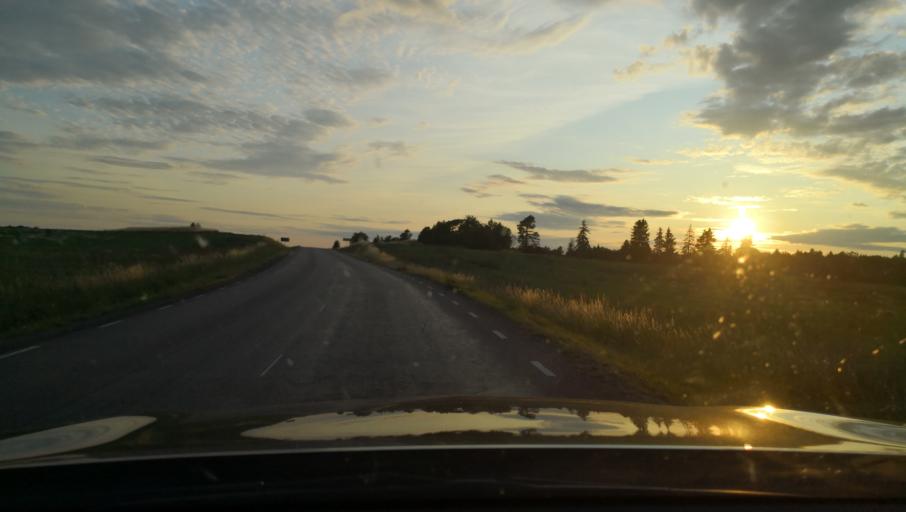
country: SE
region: Uppsala
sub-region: Uppsala Kommun
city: Vattholma
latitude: 60.0177
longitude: 17.7143
